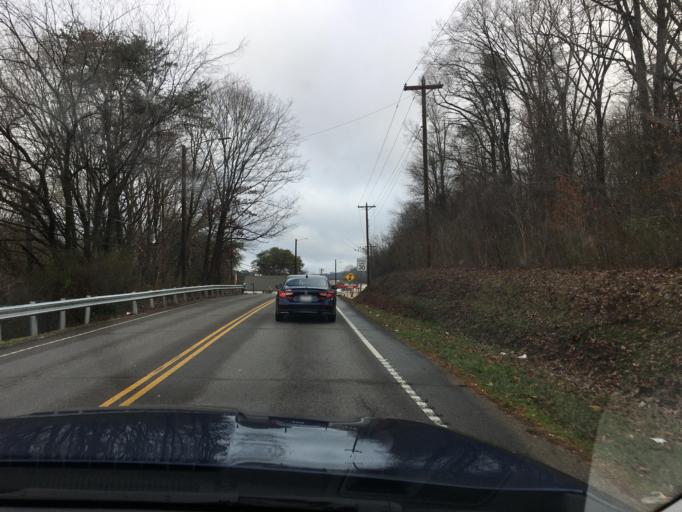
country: US
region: Tennessee
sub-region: McMinn County
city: Athens
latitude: 35.4409
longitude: -84.6115
